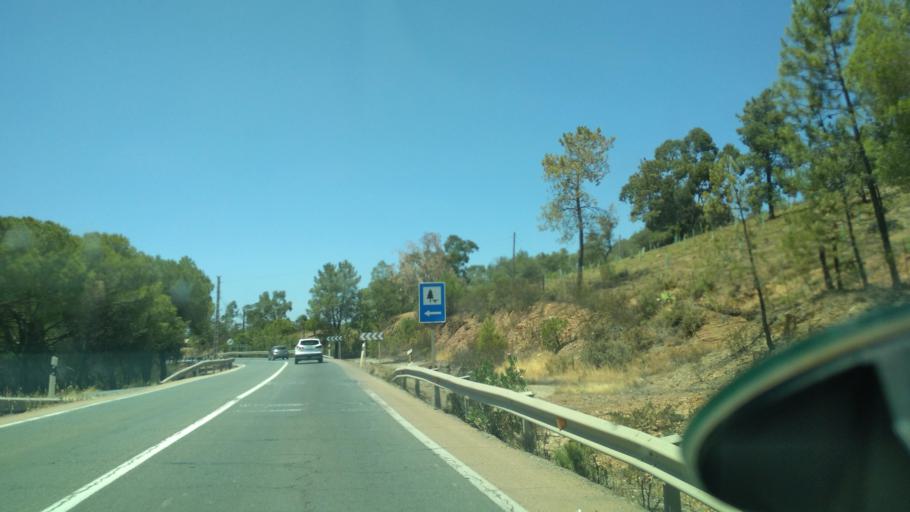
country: ES
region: Andalusia
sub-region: Provincia de Huelva
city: Zalamea la Real
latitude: 37.6916
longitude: -6.6376
